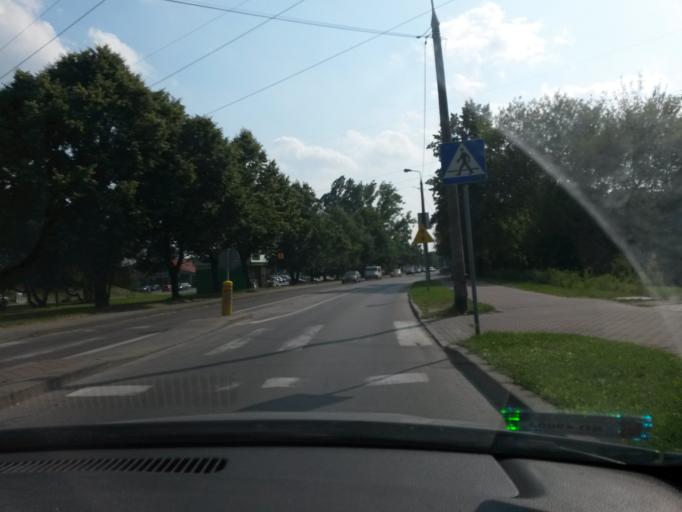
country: PL
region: Silesian Voivodeship
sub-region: Dabrowa Gornicza
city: Dabrowa Gornicza
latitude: 50.3300
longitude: 19.2248
